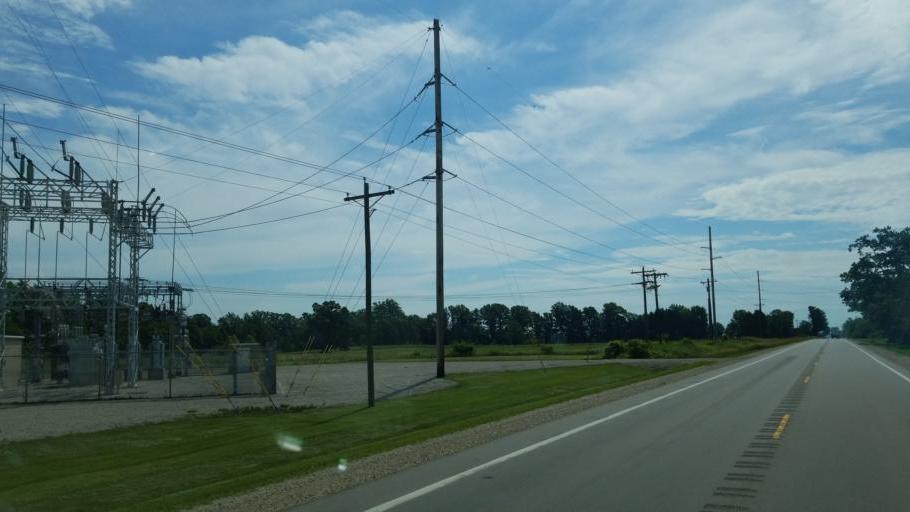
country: US
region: Michigan
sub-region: Eaton County
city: Charlotte
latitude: 42.6549
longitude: -84.9054
